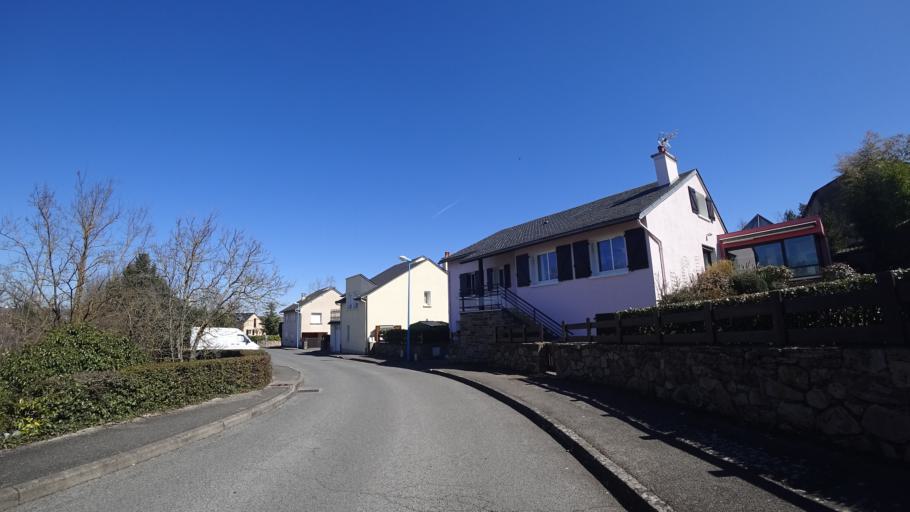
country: FR
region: Midi-Pyrenees
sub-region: Departement de l'Aveyron
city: Rodez
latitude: 44.3656
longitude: 2.5878
